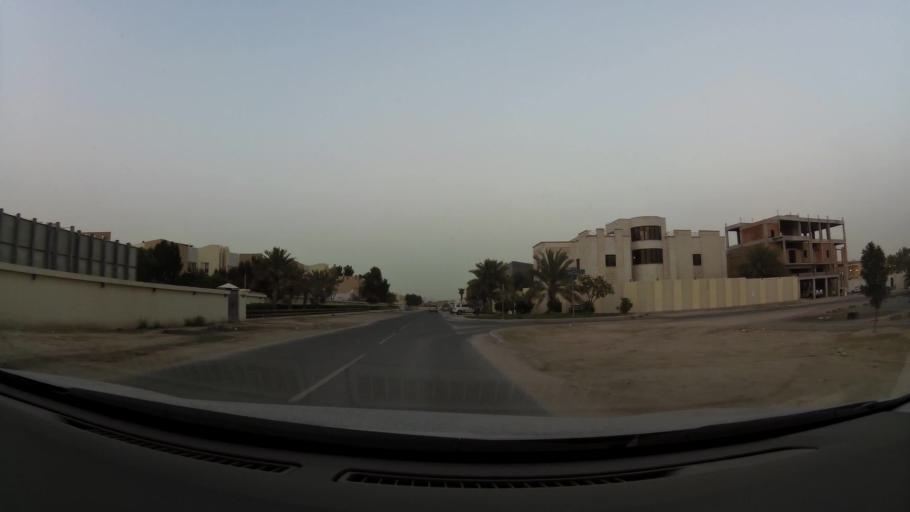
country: QA
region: Baladiyat ar Rayyan
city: Ar Rayyan
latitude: 25.2535
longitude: 51.4632
